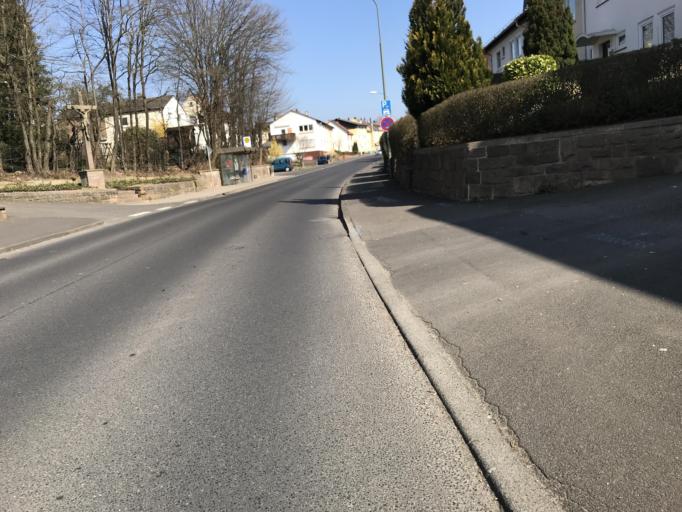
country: DE
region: Hesse
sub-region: Regierungsbezirk Kassel
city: Petersberg
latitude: 50.5557
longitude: 9.7107
